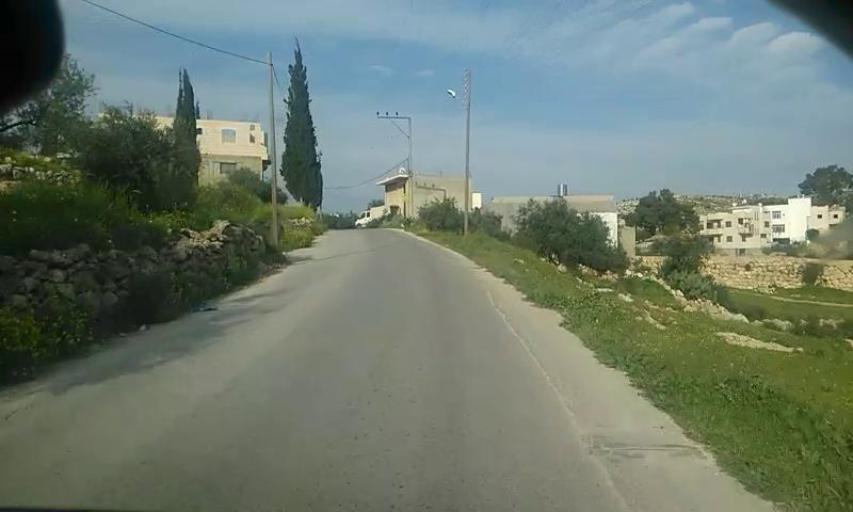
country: PS
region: West Bank
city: Bayt Ula
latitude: 31.5870
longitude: 35.0244
